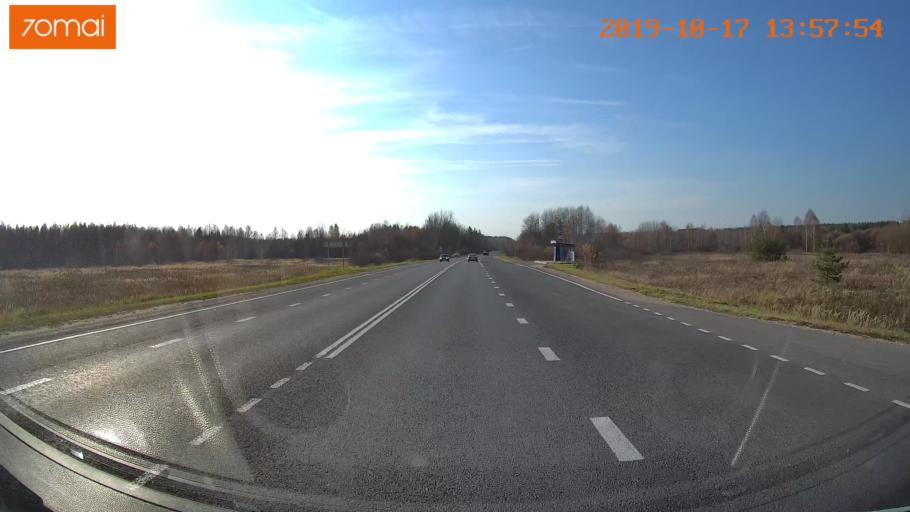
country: RU
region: Rjazan
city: Spas-Klepiki
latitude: 55.1409
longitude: 40.2367
